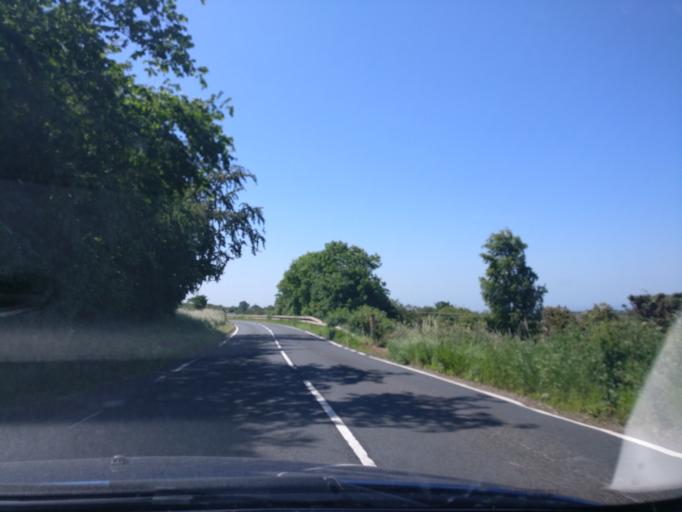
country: GB
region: Scotland
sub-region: East Lothian
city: Longniddry
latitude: 55.9857
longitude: -2.8482
